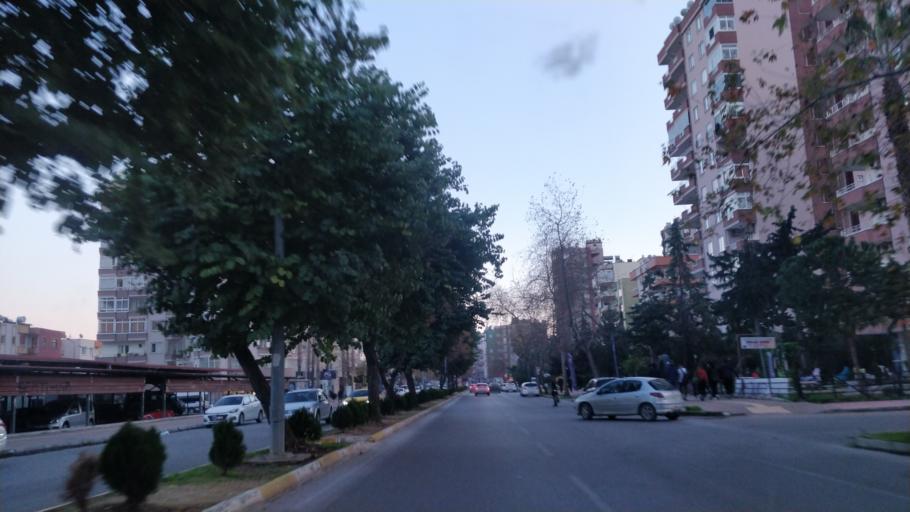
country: TR
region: Mersin
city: Mercin
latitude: 36.7887
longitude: 34.5930
